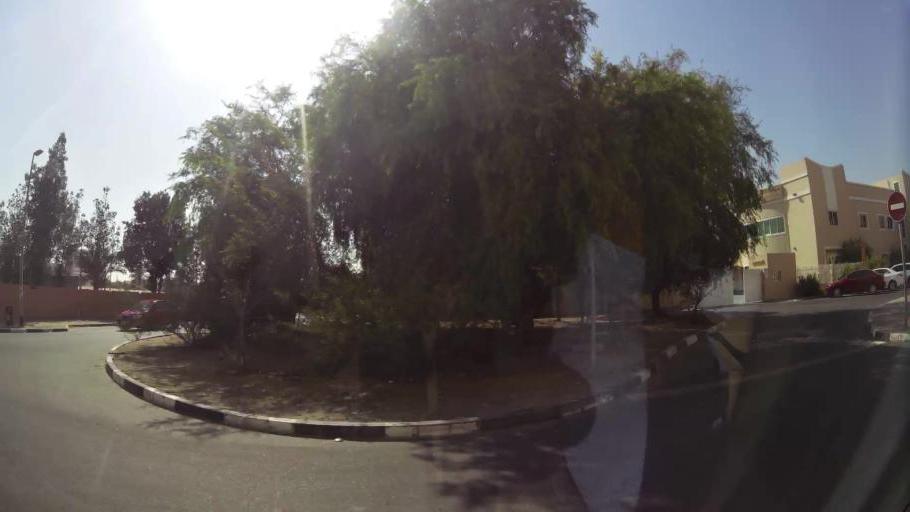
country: AE
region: Ash Shariqah
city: Sharjah
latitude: 25.2787
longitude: 55.3754
